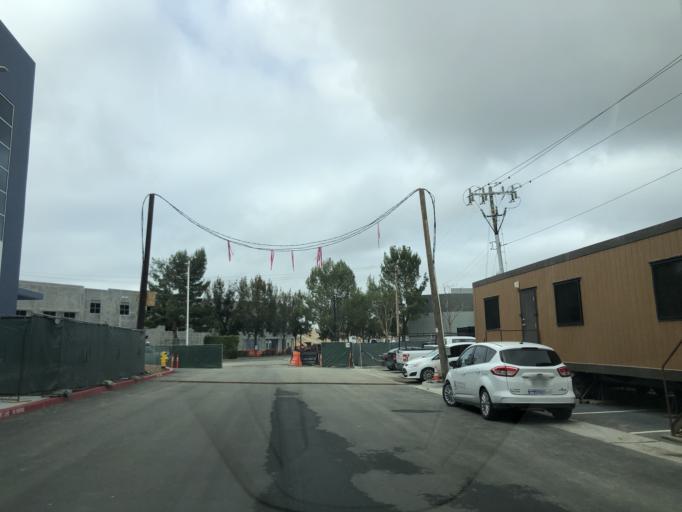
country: US
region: California
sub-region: Alameda County
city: Newark
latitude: 37.5210
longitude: -122.0316
